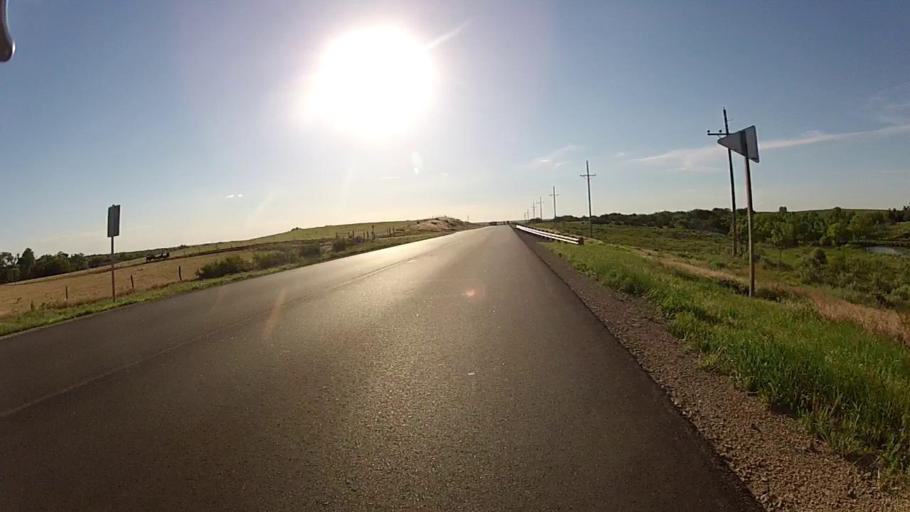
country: US
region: Kansas
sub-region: Comanche County
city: Coldwater
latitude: 37.2820
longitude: -99.0884
